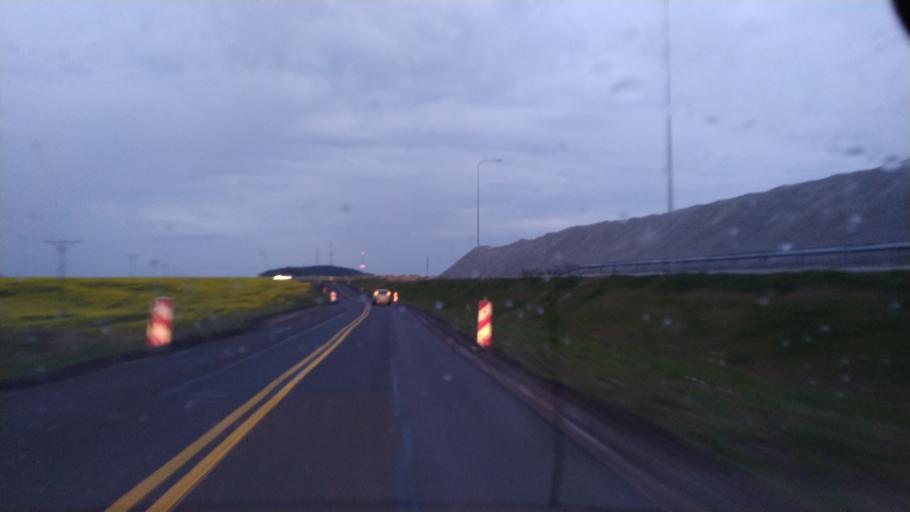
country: PL
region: Greater Poland Voivodeship
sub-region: Powiat pilski
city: Szydlowo
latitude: 53.2450
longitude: 16.6080
